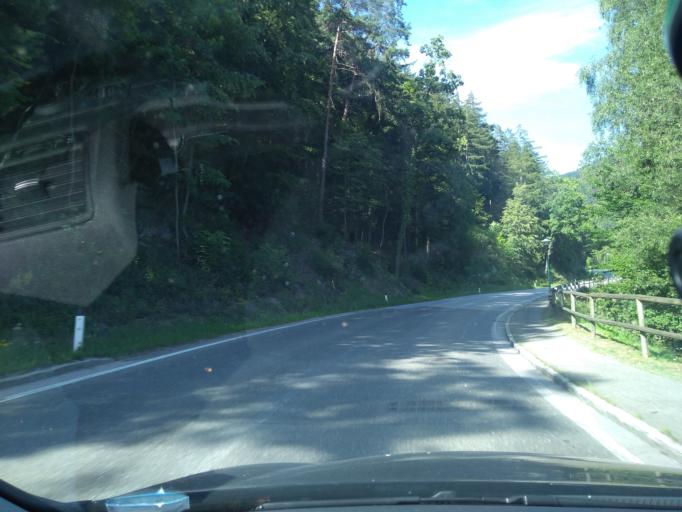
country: AT
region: Styria
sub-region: Politischer Bezirk Graz-Umgebung
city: Deutschfeistritz
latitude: 47.1711
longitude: 15.3385
